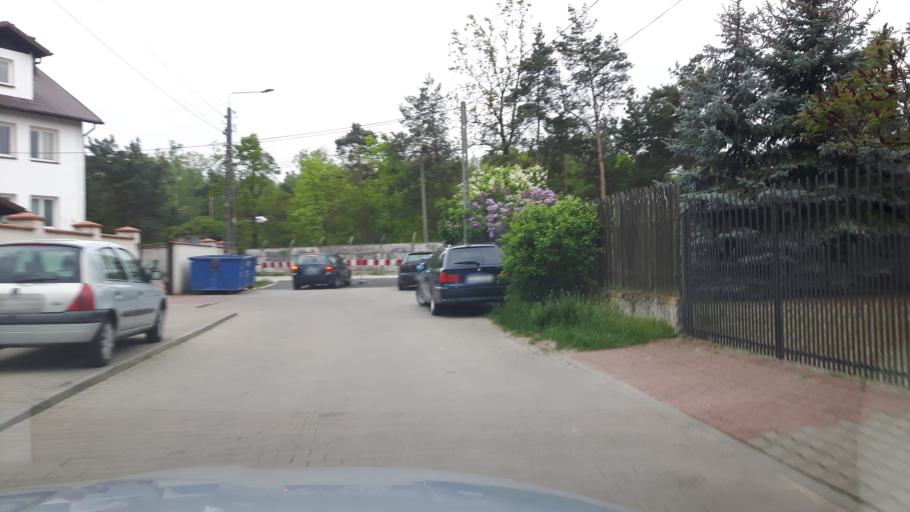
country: PL
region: Masovian Voivodeship
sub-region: Warszawa
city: Rembertow
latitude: 52.2517
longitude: 21.1620
